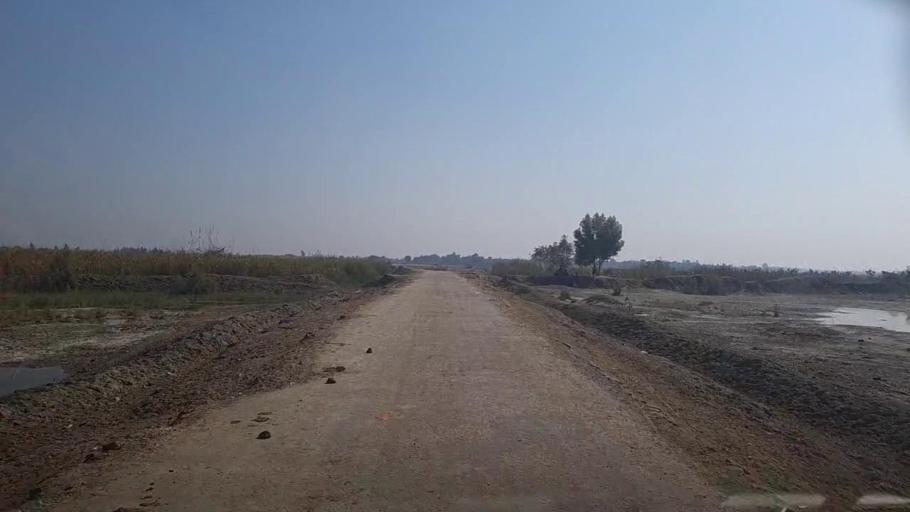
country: PK
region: Sindh
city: Kot Diji
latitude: 27.4306
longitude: 68.7277
